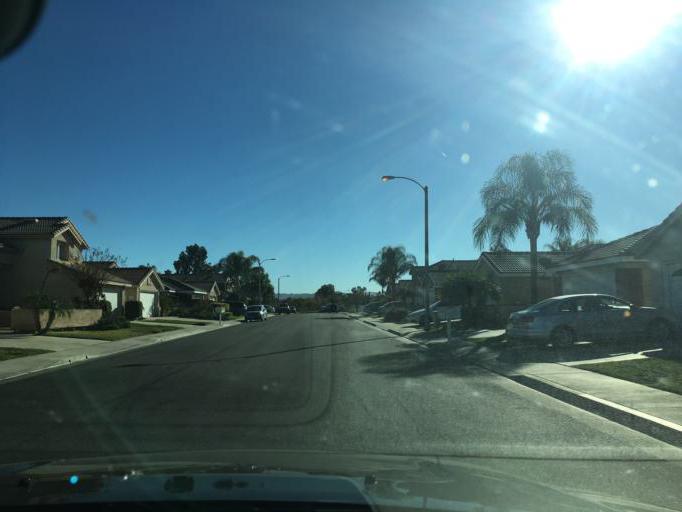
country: US
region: California
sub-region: Riverside County
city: Corona
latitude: 33.8490
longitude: -117.5548
